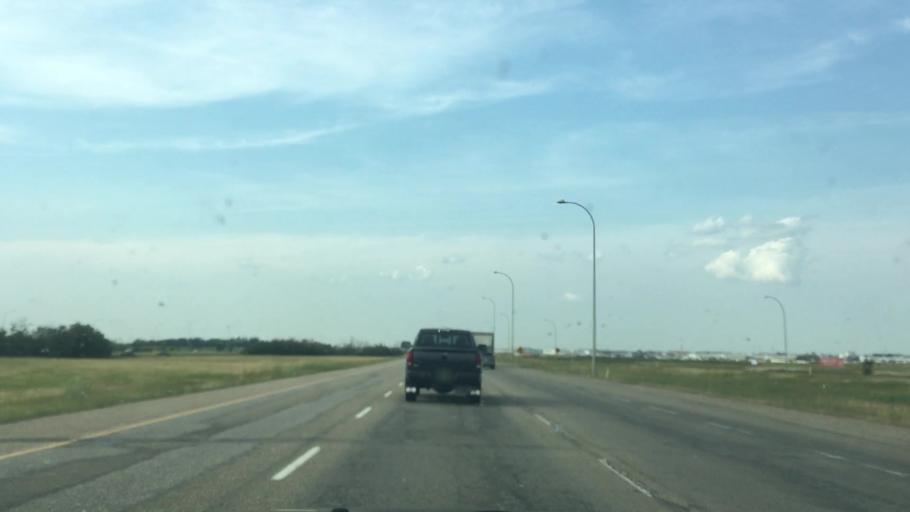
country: CA
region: Alberta
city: Leduc
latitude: 53.3115
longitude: -113.5479
